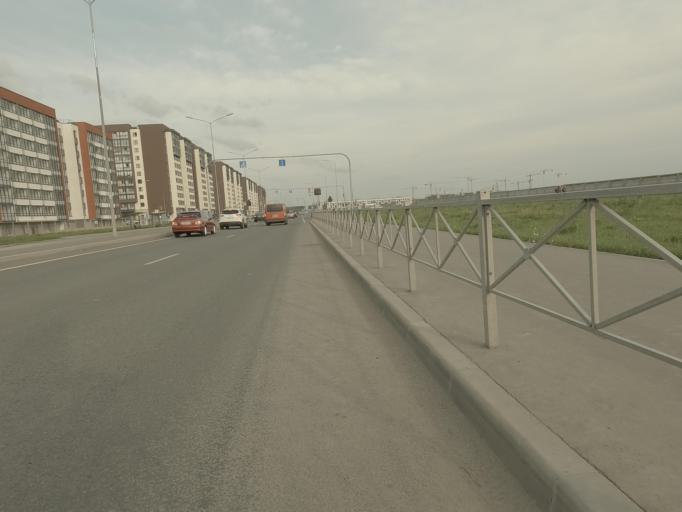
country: RU
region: St.-Petersburg
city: Sosnovaya Polyana
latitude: 59.8385
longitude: 30.1003
